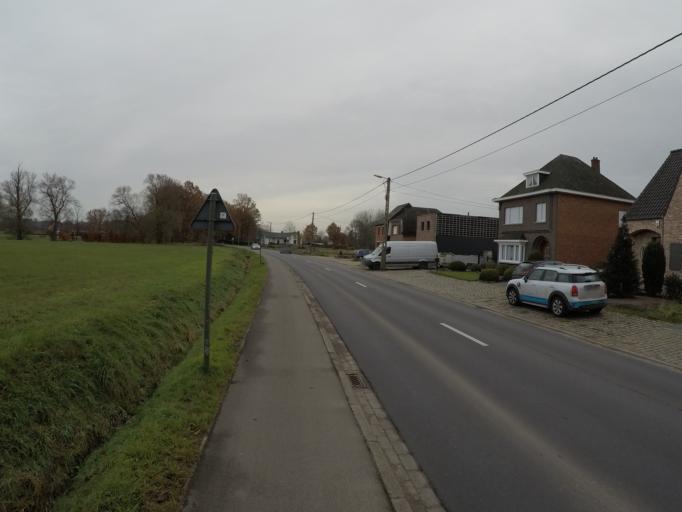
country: BE
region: Flanders
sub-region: Provincie Antwerpen
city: Berlaar
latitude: 51.1086
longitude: 4.6788
